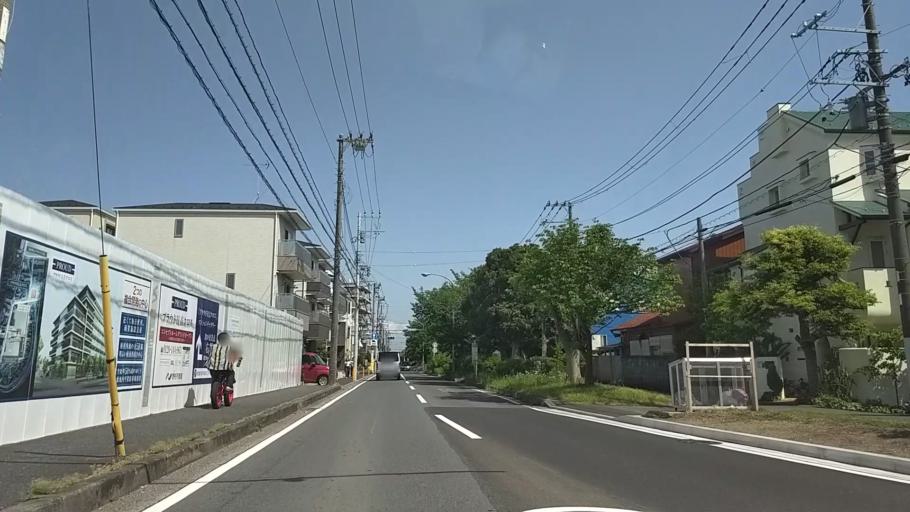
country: JP
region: Kanagawa
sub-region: Kawasaki-shi
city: Kawasaki
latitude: 35.5428
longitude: 139.6431
